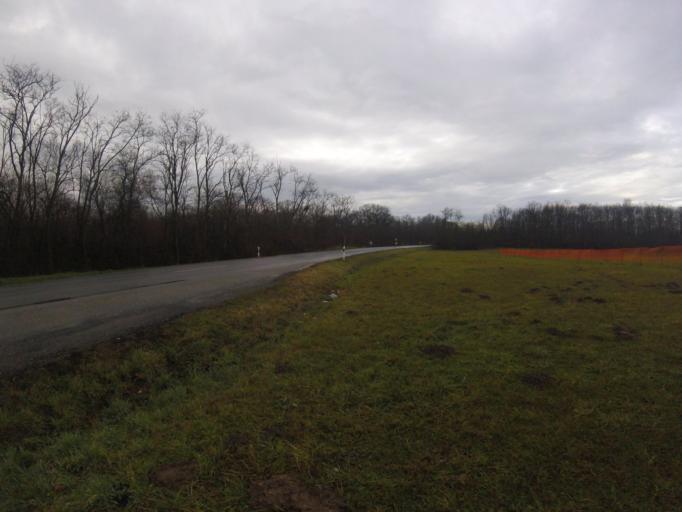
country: HU
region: Vas
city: Sarvar
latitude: 47.2385
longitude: 17.0085
